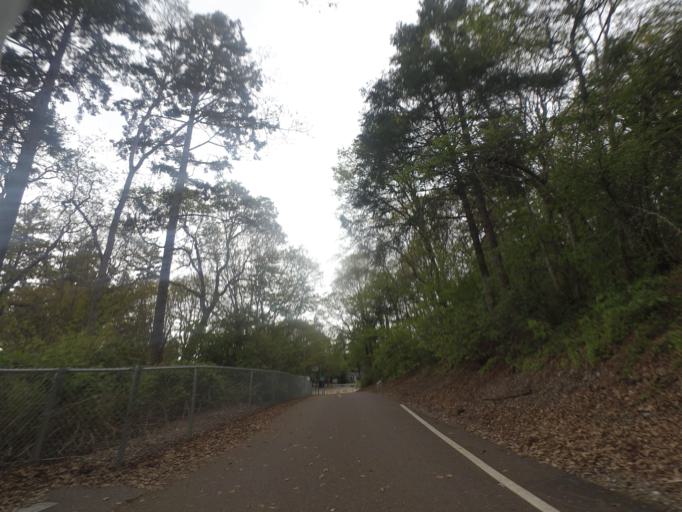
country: US
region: Washington
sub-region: Pierce County
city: Lakewood
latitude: 47.1879
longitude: -122.4769
